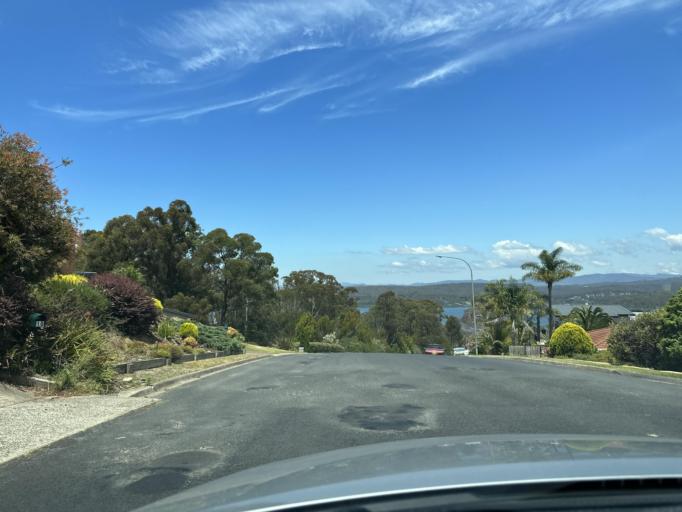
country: AU
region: New South Wales
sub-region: Bega Valley
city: Merimbula
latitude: -36.8908
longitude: 149.8964
